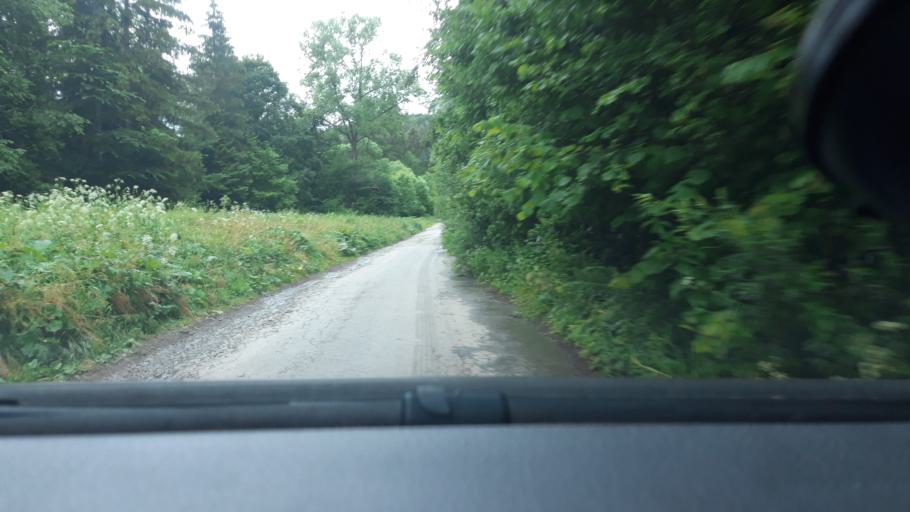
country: SK
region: Zilinsky
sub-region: Okres Martin
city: Martin
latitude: 49.0129
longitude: 19.0200
